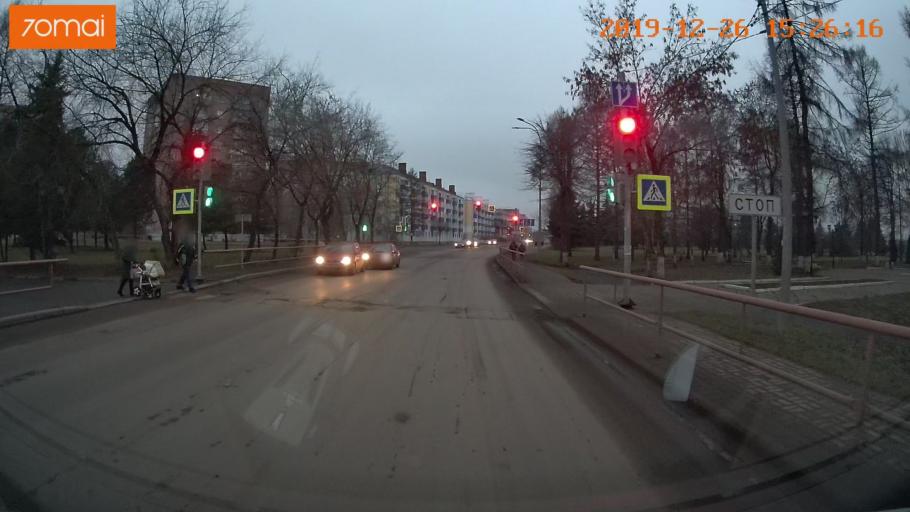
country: RU
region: Jaroslavl
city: Rybinsk
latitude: 58.0564
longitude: 38.8296
